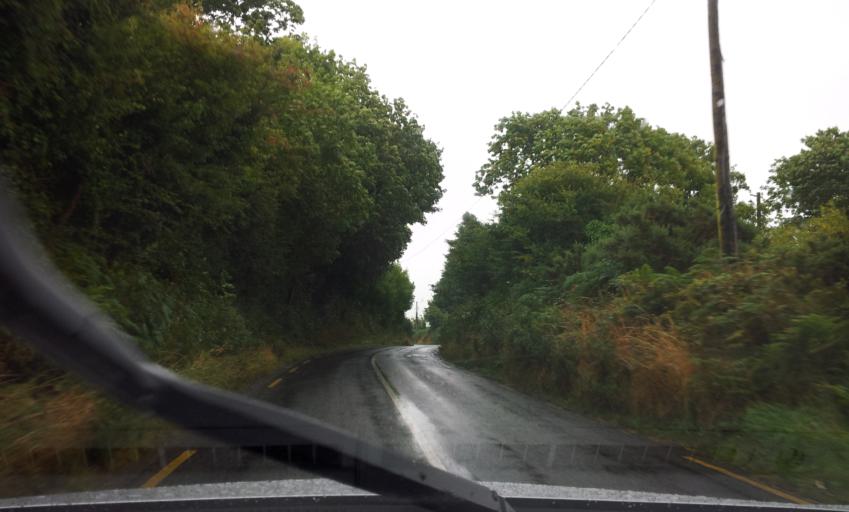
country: IE
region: Leinster
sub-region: Loch Garman
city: New Ross
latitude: 52.4082
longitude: -7.0374
